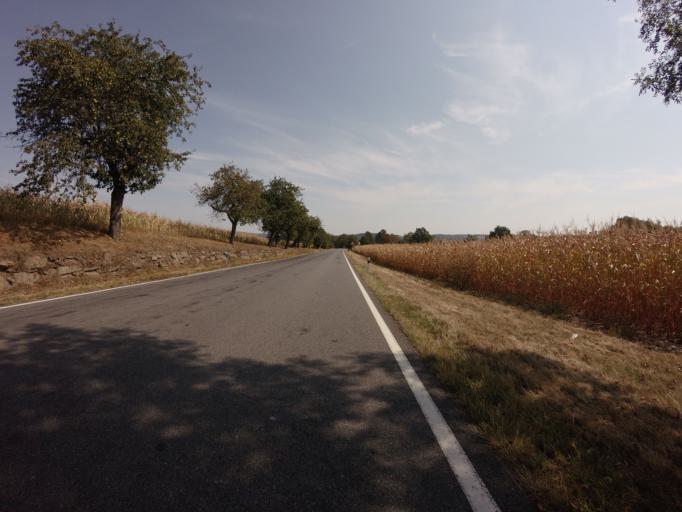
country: CZ
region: Central Bohemia
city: Sedlcany
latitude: 49.6216
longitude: 14.4211
